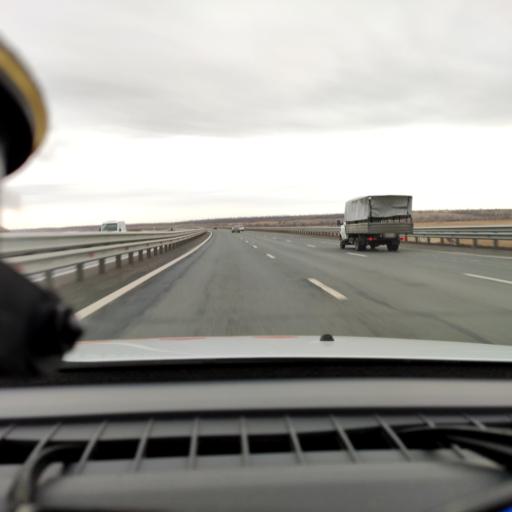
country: RU
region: Samara
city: Smyshlyayevka
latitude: 53.1619
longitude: 50.3256
